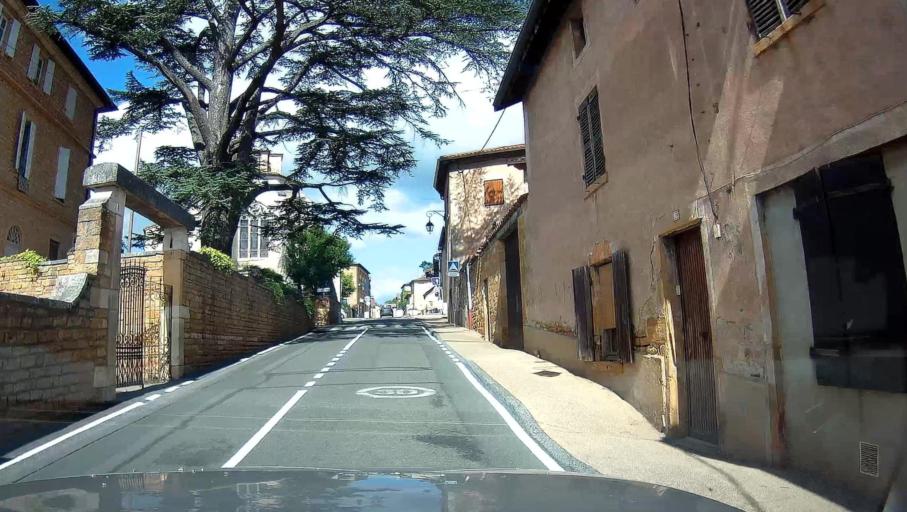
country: FR
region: Rhone-Alpes
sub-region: Departement du Rhone
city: Liergues
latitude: 45.9694
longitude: 4.6652
